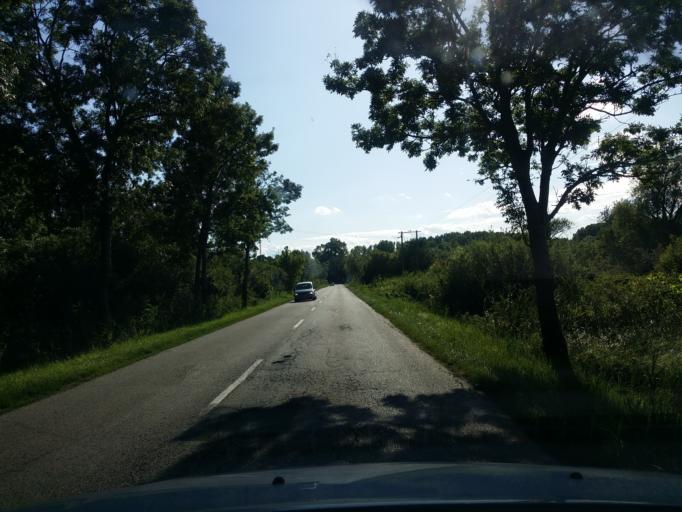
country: HU
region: Fejer
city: Sarbogard
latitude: 46.8496
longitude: 18.5690
